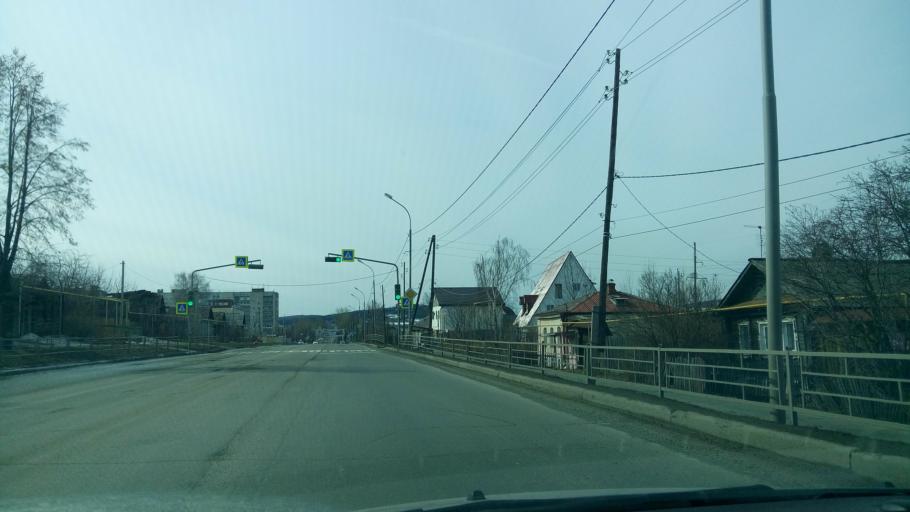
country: RU
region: Sverdlovsk
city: Nizhniy Tagil
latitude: 57.9009
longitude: 59.9422
